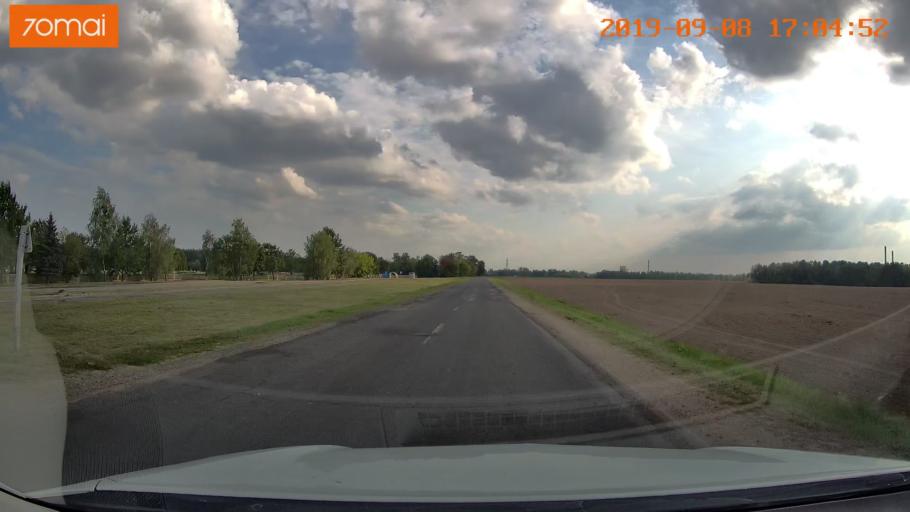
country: BY
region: Grodnenskaya
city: Hrodna
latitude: 53.6852
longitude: 23.9556
